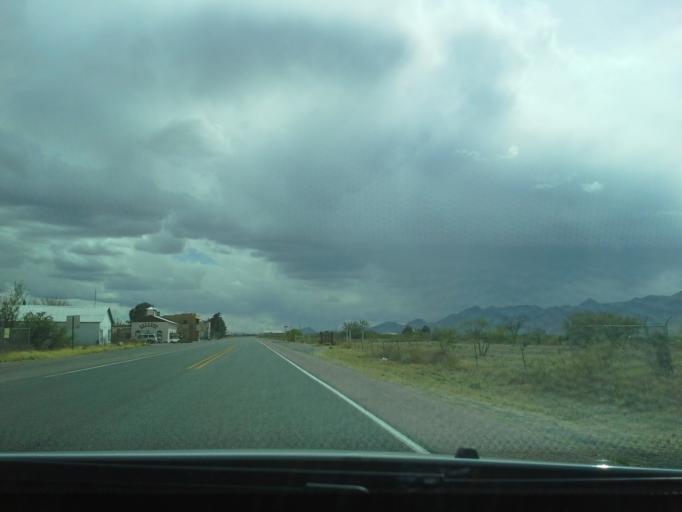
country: US
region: New Mexico
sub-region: Hidalgo County
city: Lordsburg
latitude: 31.8369
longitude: -109.0309
